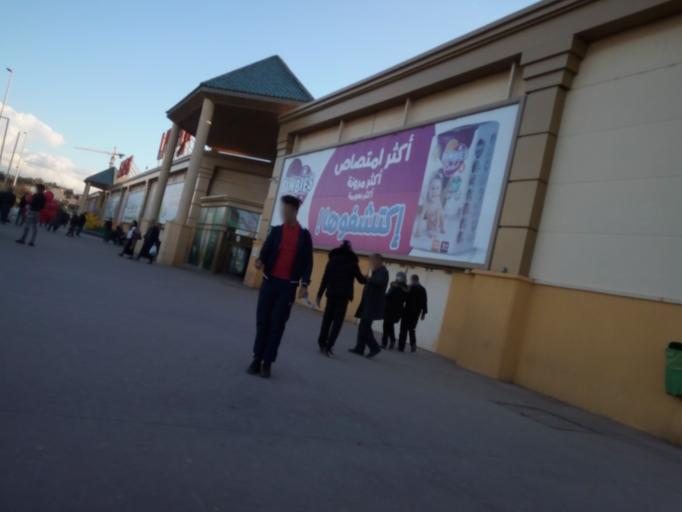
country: DZ
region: Alger
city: Bab Ezzouar
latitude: 36.7394
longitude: 3.1435
